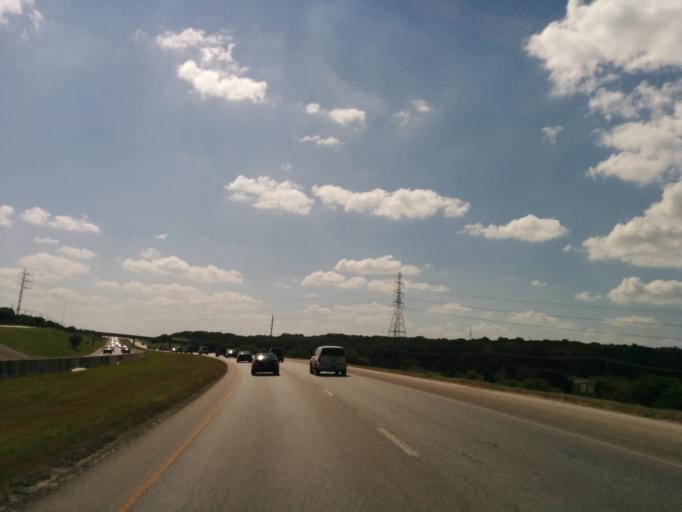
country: US
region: Texas
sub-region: Bexar County
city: Live Oak
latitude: 29.6028
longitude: -98.3615
